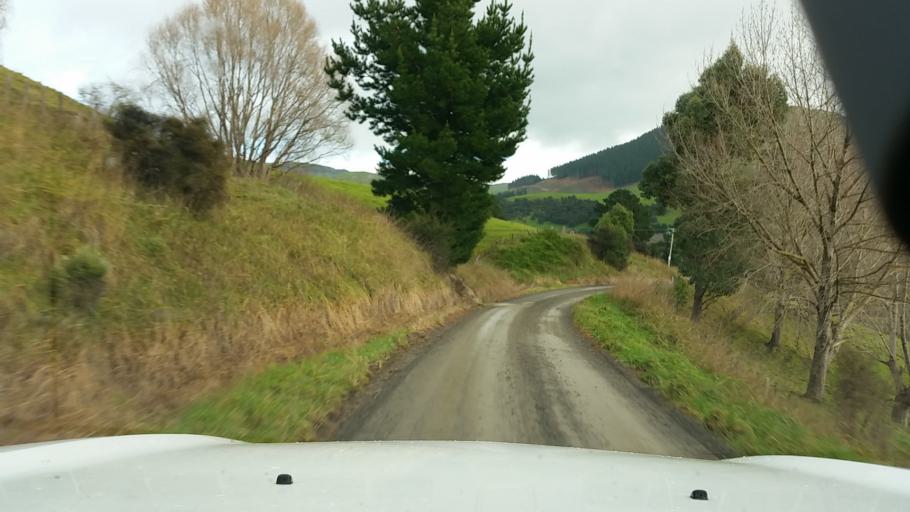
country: NZ
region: Wellington
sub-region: South Wairarapa District
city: Waipawa
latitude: -41.2153
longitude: 175.5762
